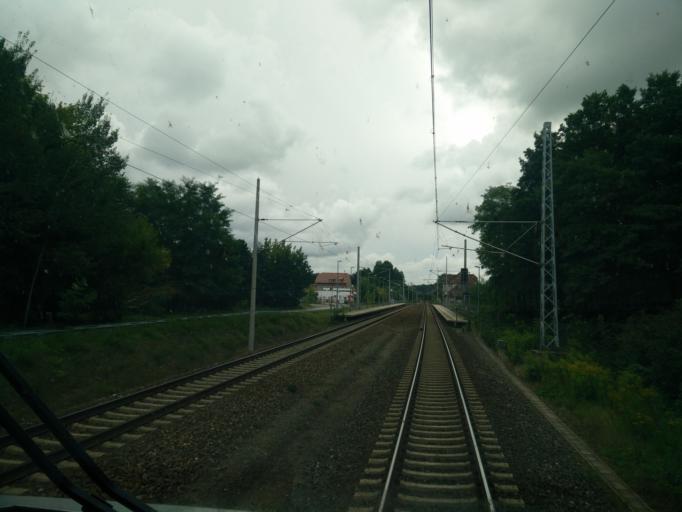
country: DE
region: Brandenburg
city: Gross Koris
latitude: 52.1611
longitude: 13.6499
